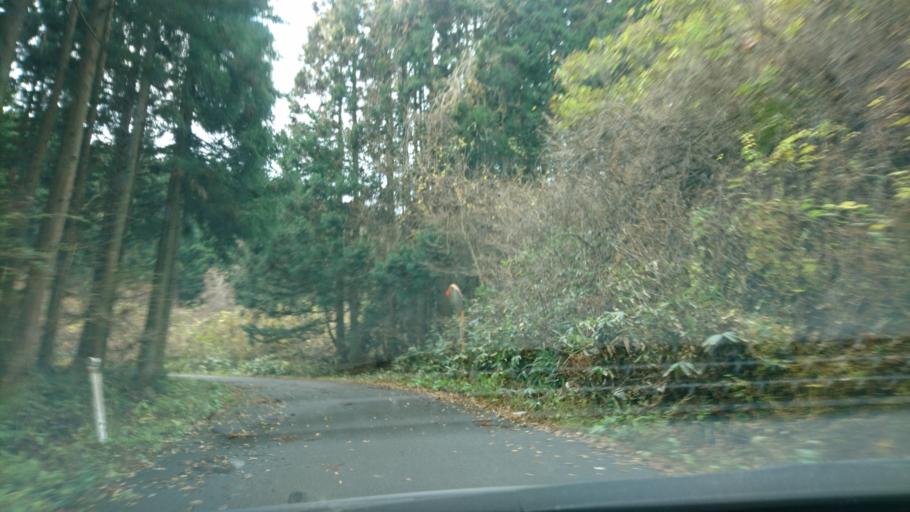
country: JP
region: Iwate
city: Ichinoseki
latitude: 39.0043
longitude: 141.1960
